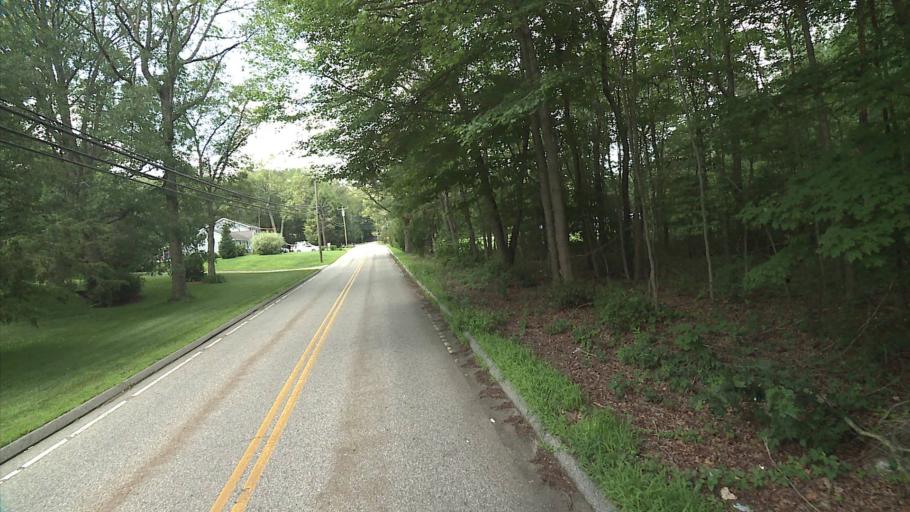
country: US
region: Connecticut
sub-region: New London County
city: Baltic
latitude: 41.6146
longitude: -72.0519
